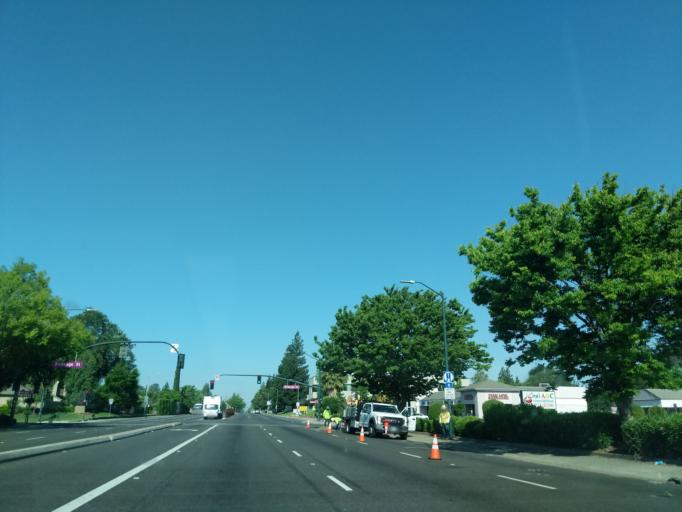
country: US
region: California
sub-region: Sacramento County
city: Citrus Heights
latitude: 38.6784
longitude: -121.2751
